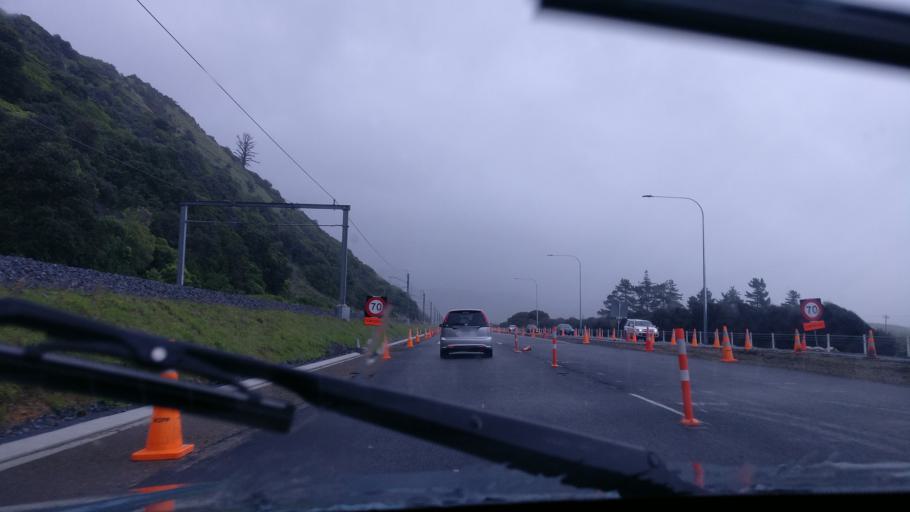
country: NZ
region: Wellington
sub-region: Kapiti Coast District
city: Paraparaumu
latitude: -40.9453
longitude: 174.9912
